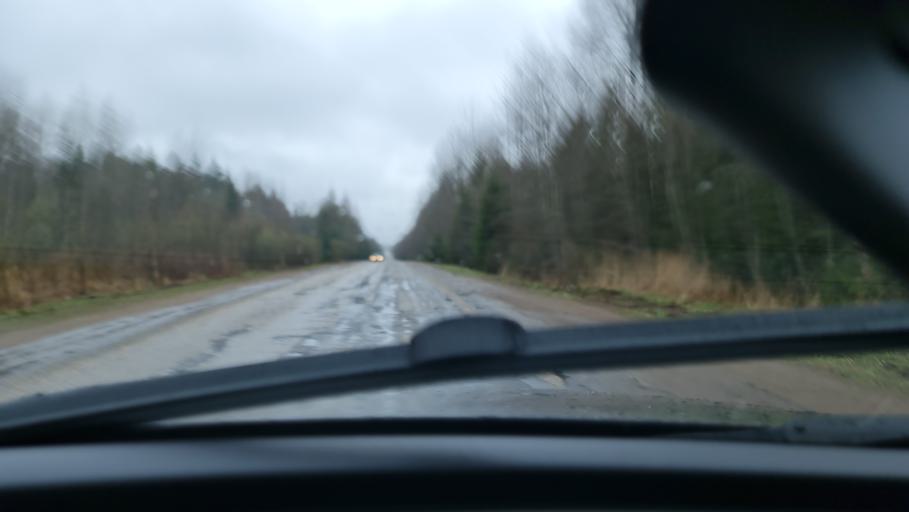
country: RU
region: Novgorod
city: Valday
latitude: 58.0355
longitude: 32.8701
